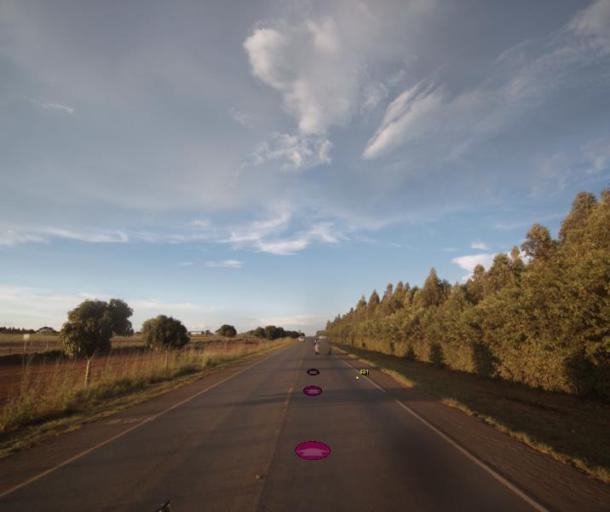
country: BR
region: Goias
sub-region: Anapolis
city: Anapolis
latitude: -16.2144
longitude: -48.9186
